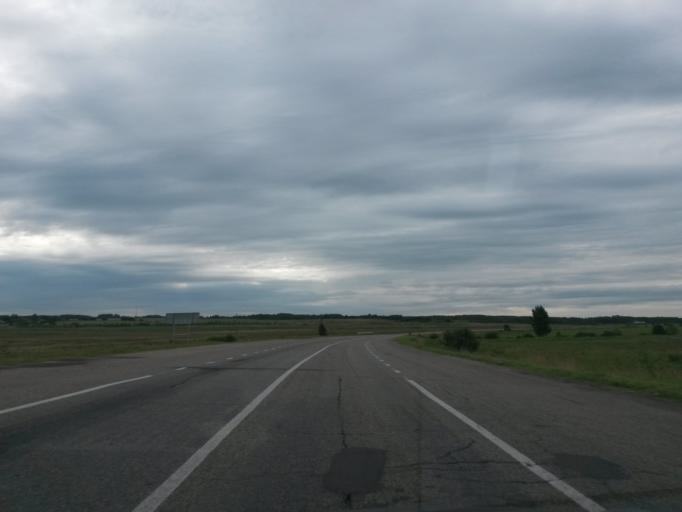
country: RU
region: Jaroslavl
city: Gavrilov-Yam
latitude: 57.3158
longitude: 39.8787
